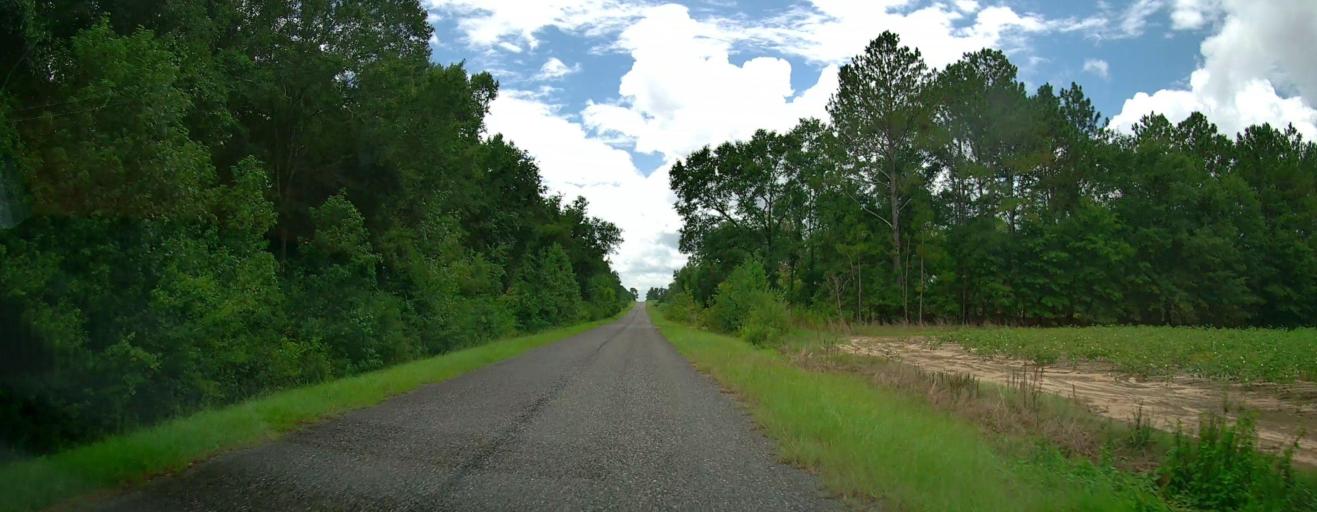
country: US
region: Georgia
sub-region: Dooly County
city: Vienna
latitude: 32.0556
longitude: -83.6278
